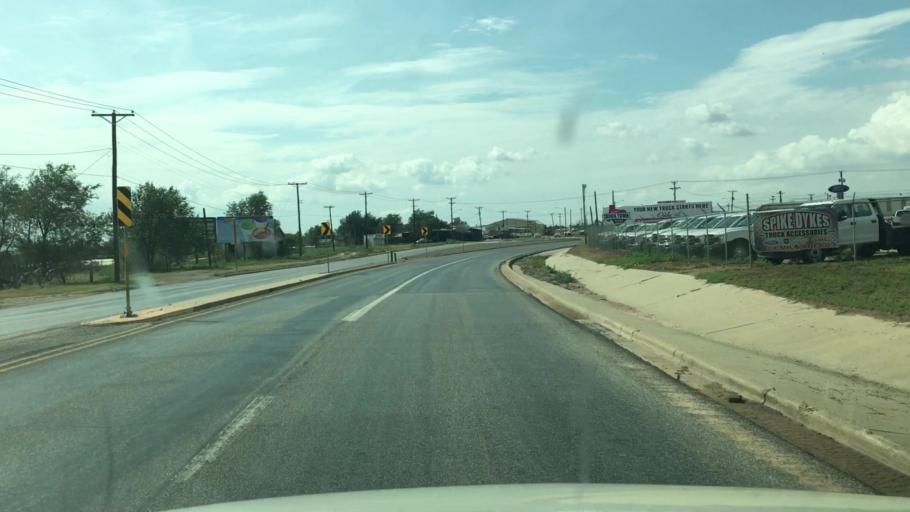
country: US
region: Texas
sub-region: Dawson County
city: Lamesa
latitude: 32.7191
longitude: -101.9440
